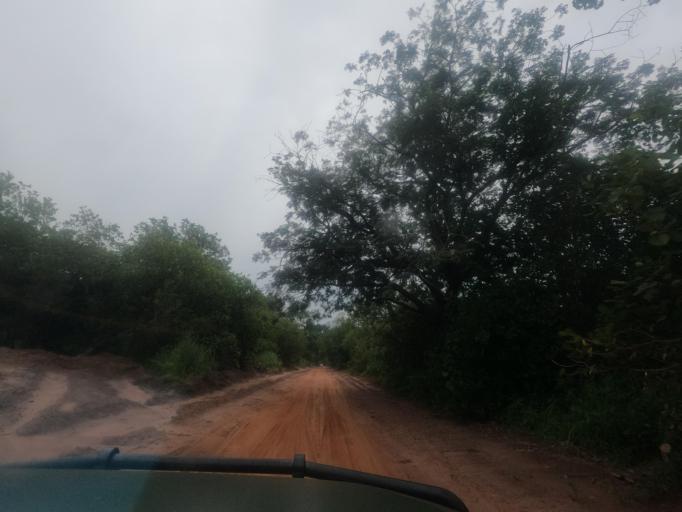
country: GW
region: Oio
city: Bissora
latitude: 12.4065
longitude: -15.7255
